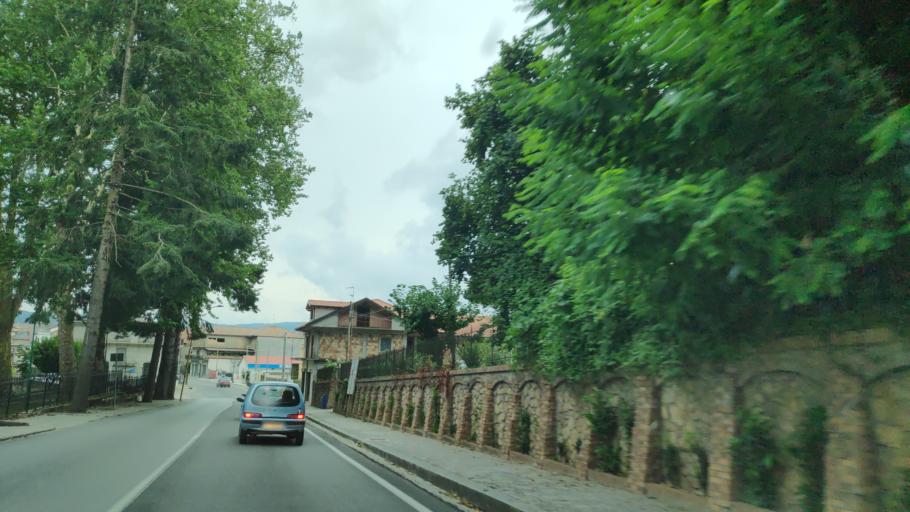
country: IT
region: Calabria
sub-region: Provincia di Vibo-Valentia
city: Serra San Bruno
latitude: 38.5827
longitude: 16.3339
